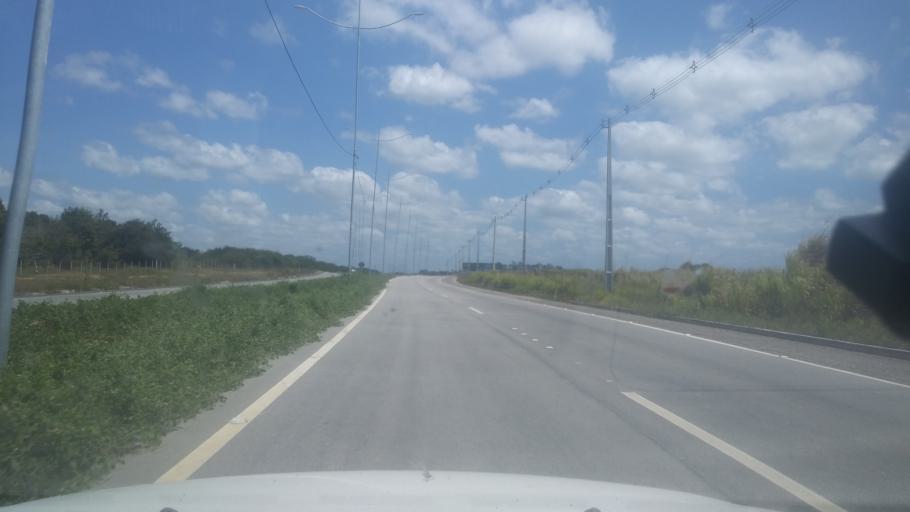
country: BR
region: Rio Grande do Norte
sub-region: Macaiba
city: Macaiba
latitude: -5.8381
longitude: -35.3750
